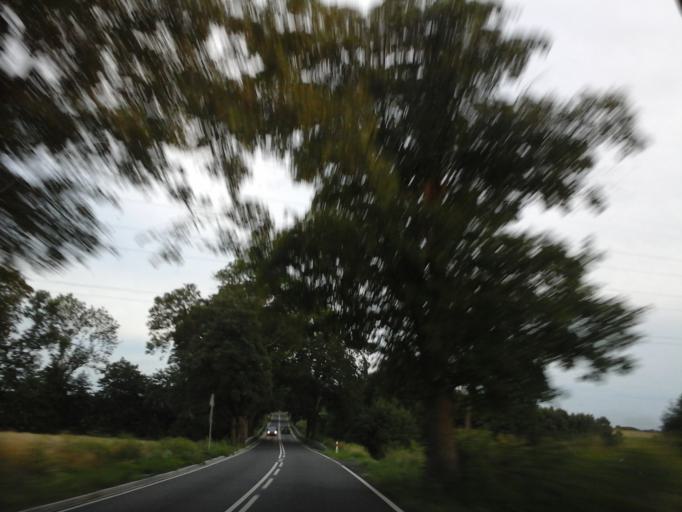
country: PL
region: West Pomeranian Voivodeship
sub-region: Powiat stargardzki
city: Stara Dabrowa
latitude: 53.4169
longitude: 15.0903
